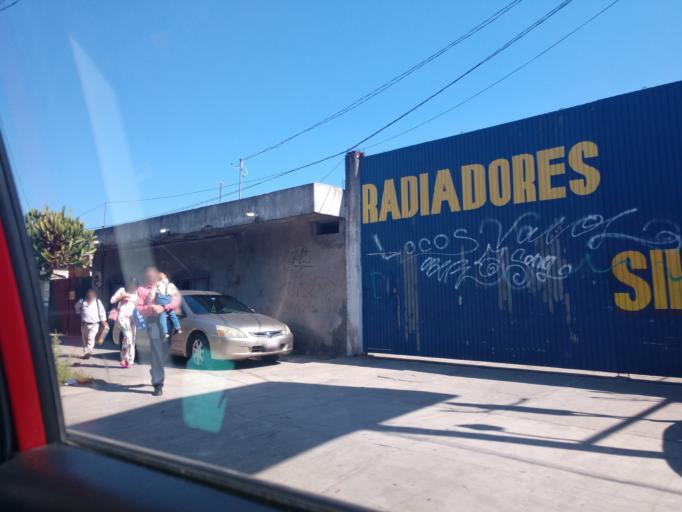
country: MX
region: Nayarit
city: Xalisco
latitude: 21.4756
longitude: -104.8692
